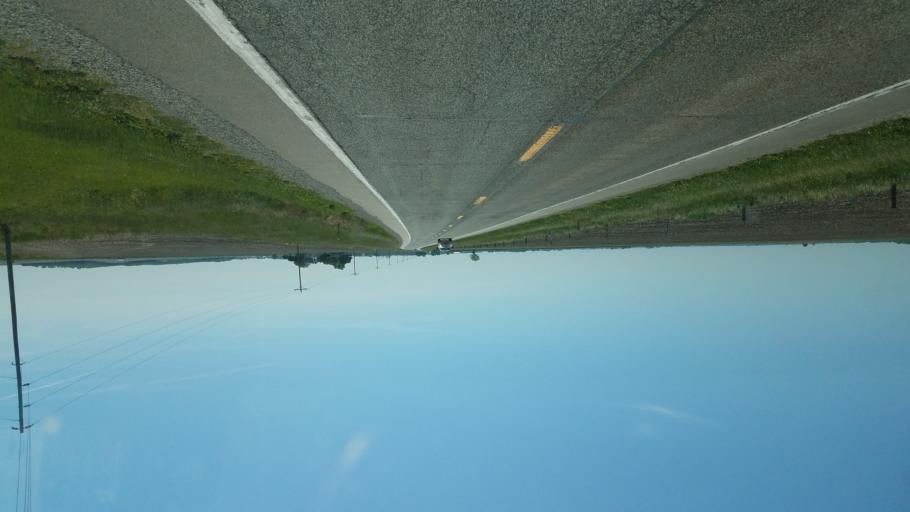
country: US
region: Illinois
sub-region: Mason County
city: Mason City
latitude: 40.3045
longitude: -89.7336
